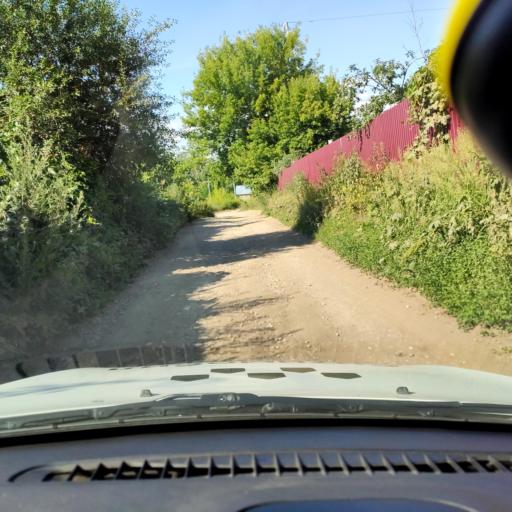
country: RU
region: Samara
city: Zhigulevsk
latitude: 53.3992
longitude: 49.5233
